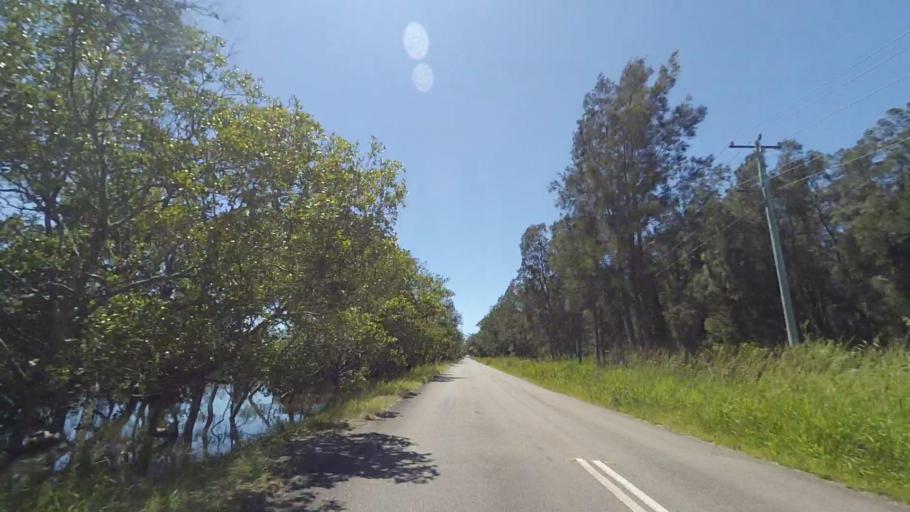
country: AU
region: New South Wales
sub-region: Port Stephens Shire
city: Medowie
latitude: -32.7800
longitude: 151.9507
